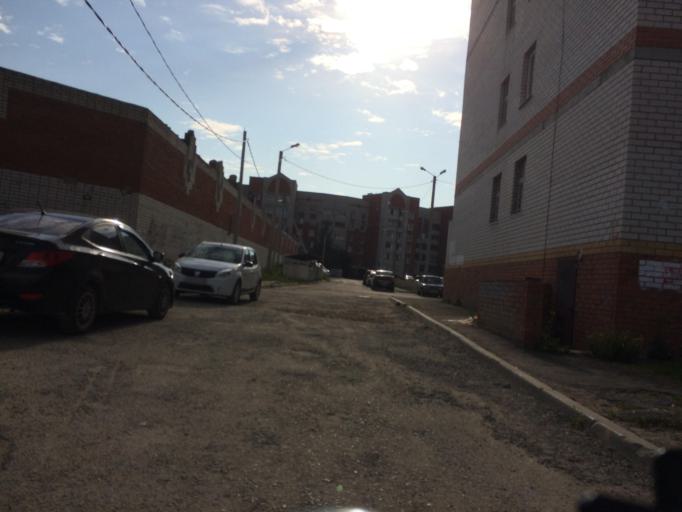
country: RU
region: Mariy-El
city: Medvedevo
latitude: 56.6382
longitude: 47.8261
